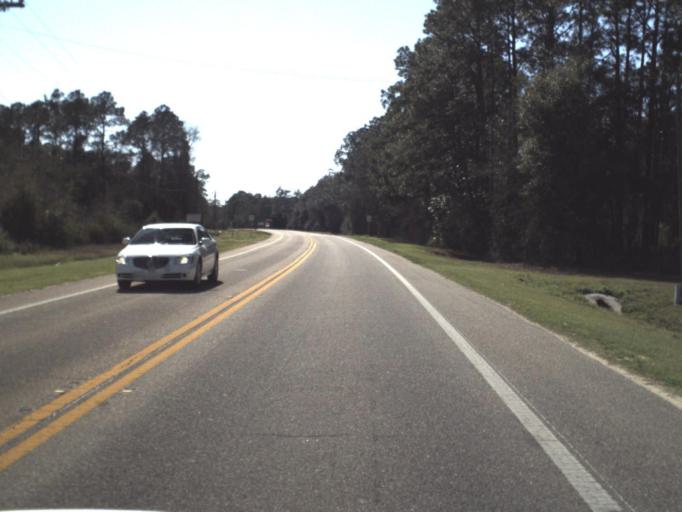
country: US
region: Florida
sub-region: Calhoun County
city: Blountstown
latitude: 30.4426
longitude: -85.0714
